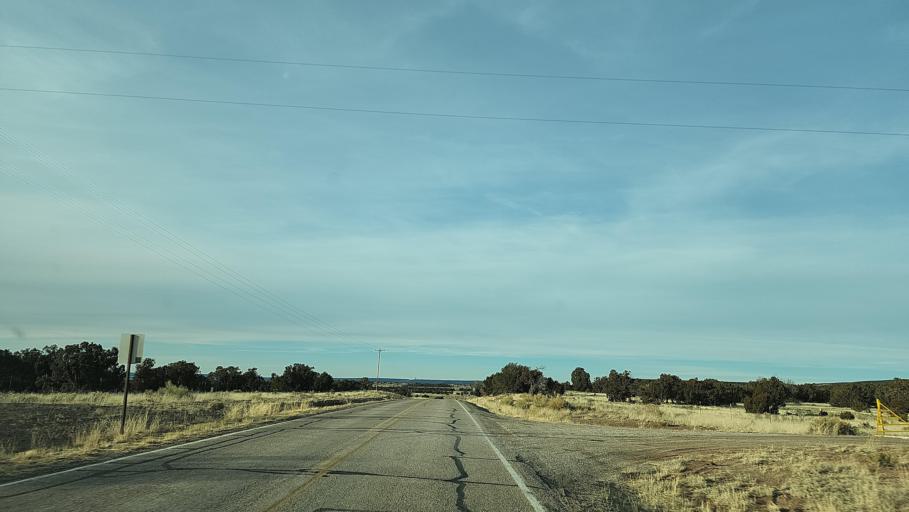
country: US
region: New Mexico
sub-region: McKinley County
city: Black Rock
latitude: 34.4354
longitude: -108.4276
